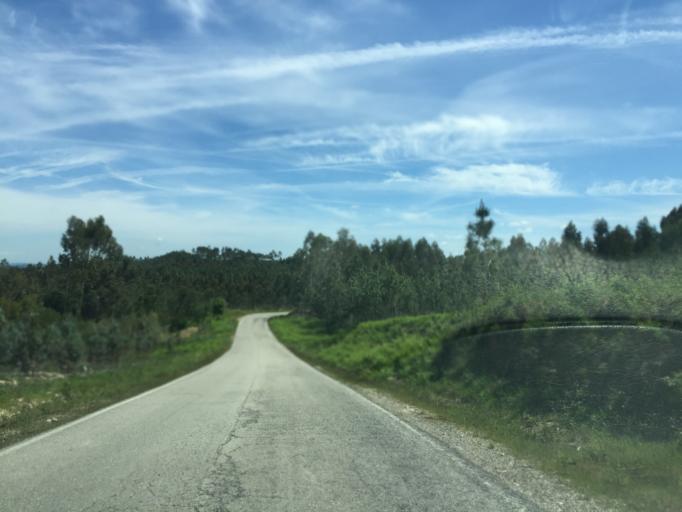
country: PT
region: Coimbra
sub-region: Soure
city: Soure
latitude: 40.0551
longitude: -8.6821
